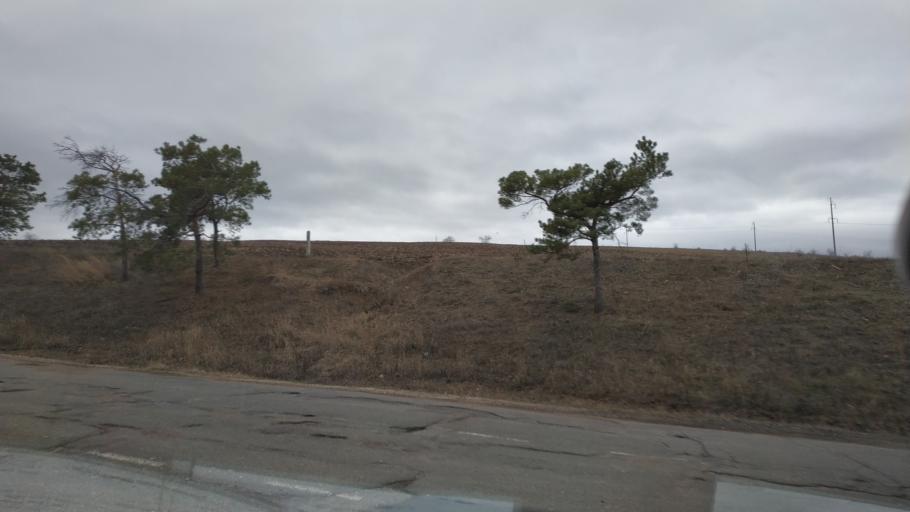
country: MD
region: Bender
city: Bender
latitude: 46.7775
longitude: 29.4752
